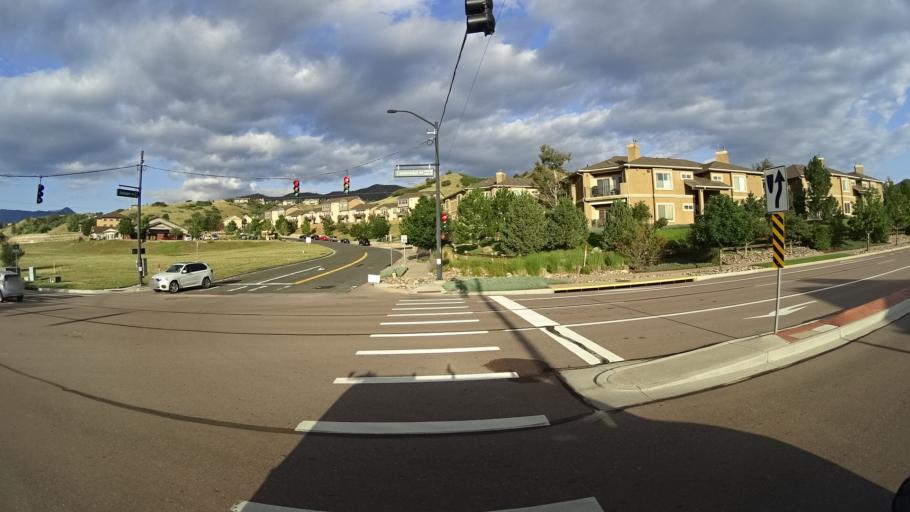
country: US
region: Colorado
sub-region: El Paso County
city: Manitou Springs
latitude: 38.9160
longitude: -104.8634
